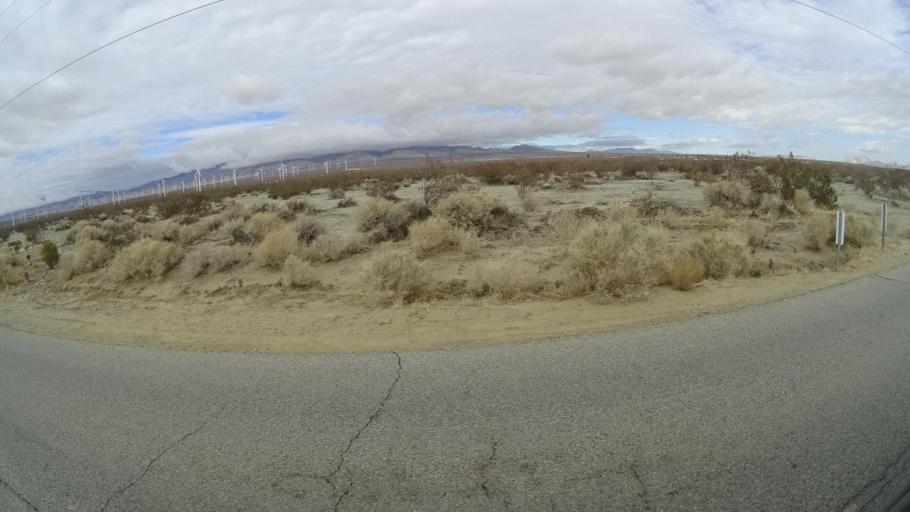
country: US
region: California
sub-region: Kern County
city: Rosamond
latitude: 34.8628
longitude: -118.3960
